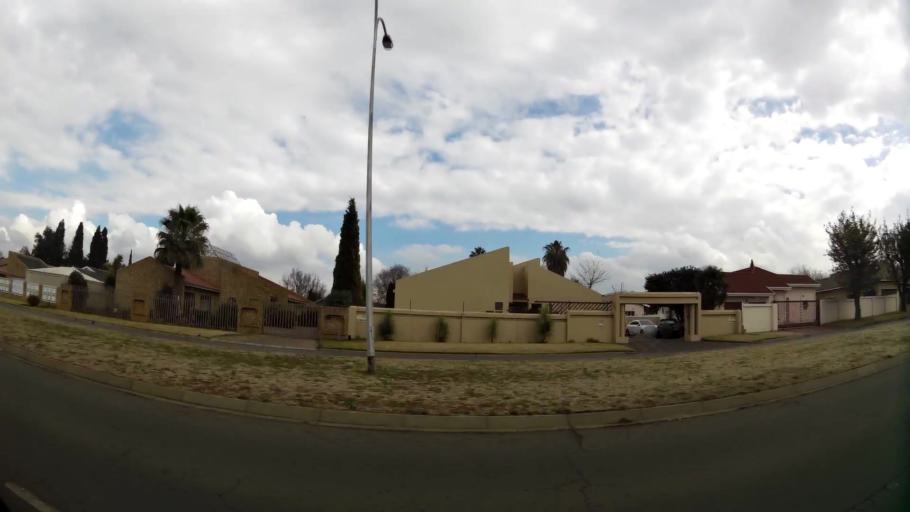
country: ZA
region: Gauteng
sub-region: Sedibeng District Municipality
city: Vanderbijlpark
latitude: -26.7343
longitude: 27.8544
